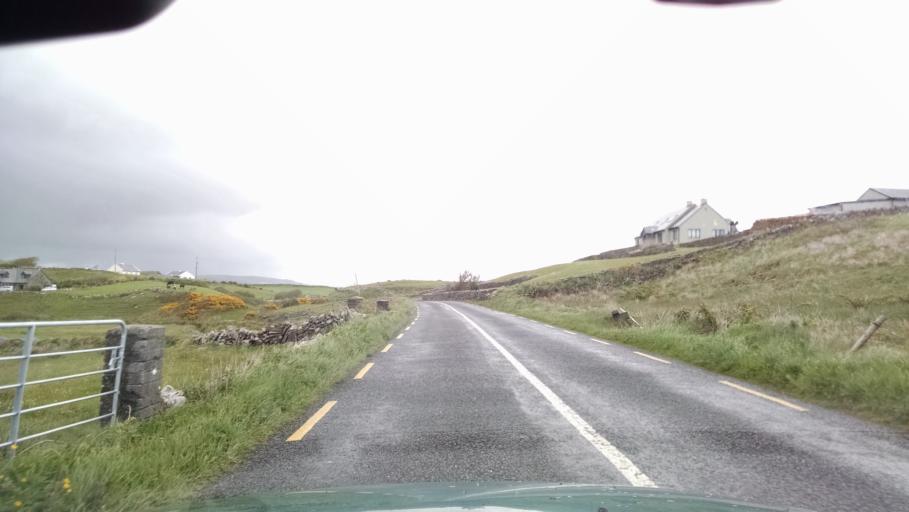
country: IE
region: Connaught
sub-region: County Galway
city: Bearna
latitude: 53.0092
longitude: -9.3499
